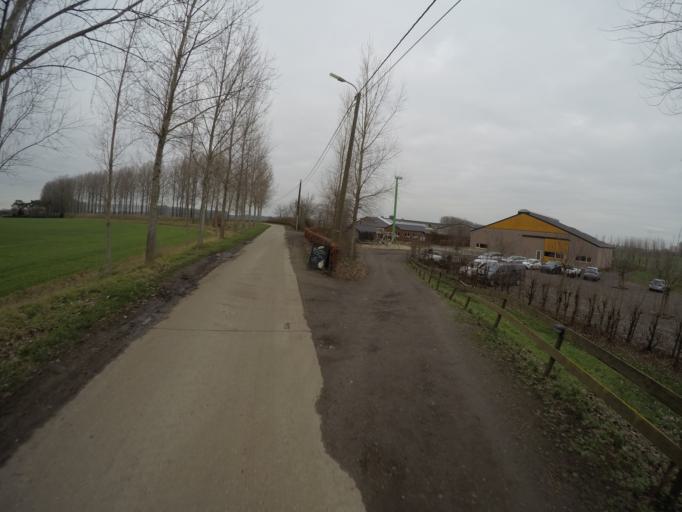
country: BE
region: Flanders
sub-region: Provincie Oost-Vlaanderen
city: Sint-Gillis-Waas
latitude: 51.2453
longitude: 4.1250
